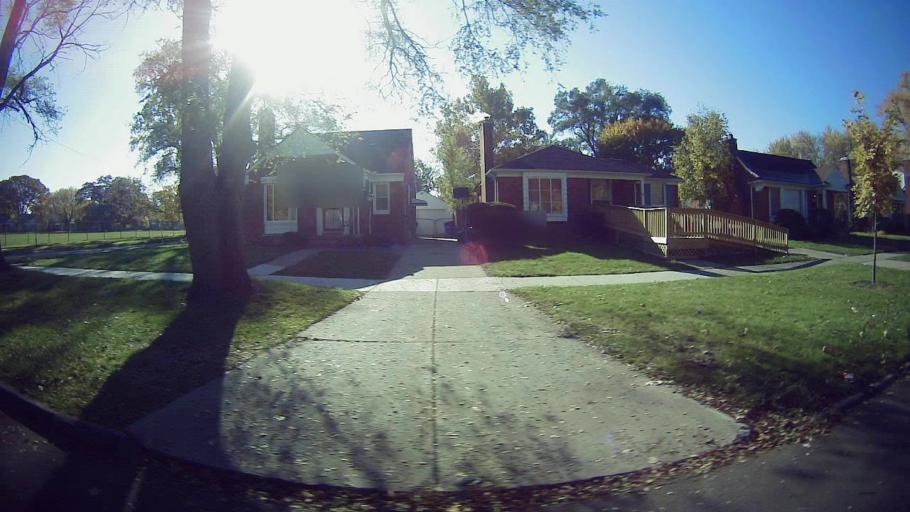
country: US
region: Michigan
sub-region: Wayne County
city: Dearborn Heights
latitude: 42.3491
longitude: -83.2618
